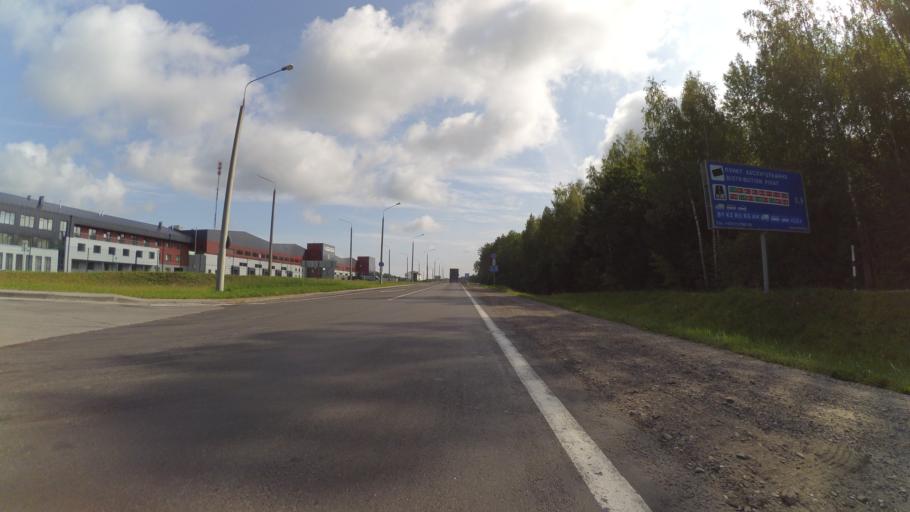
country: PL
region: Podlasie
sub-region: Powiat sokolski
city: Kuznica
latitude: 53.5262
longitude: 23.6747
